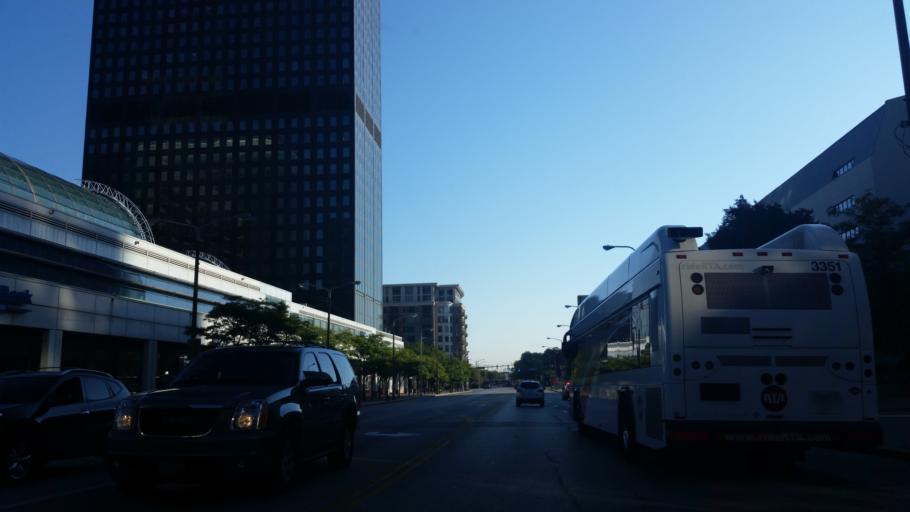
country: US
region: Ohio
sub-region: Cuyahoga County
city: Cleveland
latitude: 41.5039
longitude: -81.6899
